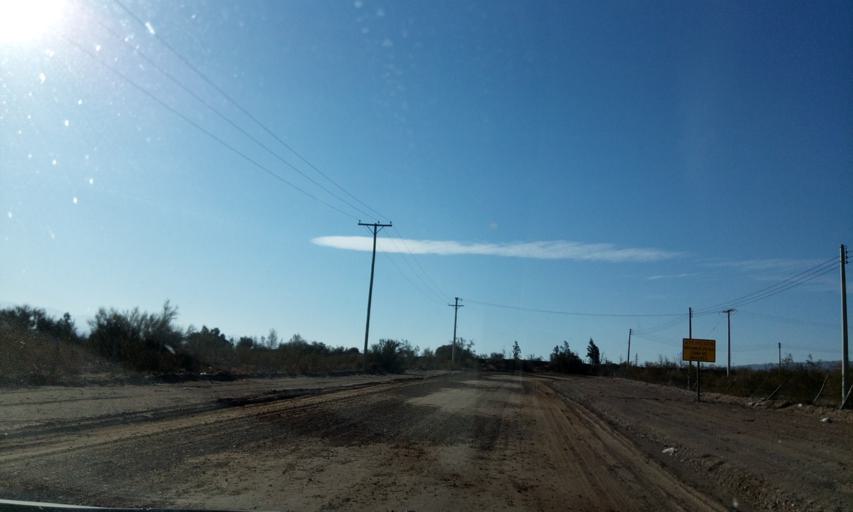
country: AR
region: San Juan
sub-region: Departamento de Rivadavia
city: Rivadavia
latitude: -31.4258
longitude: -68.6719
